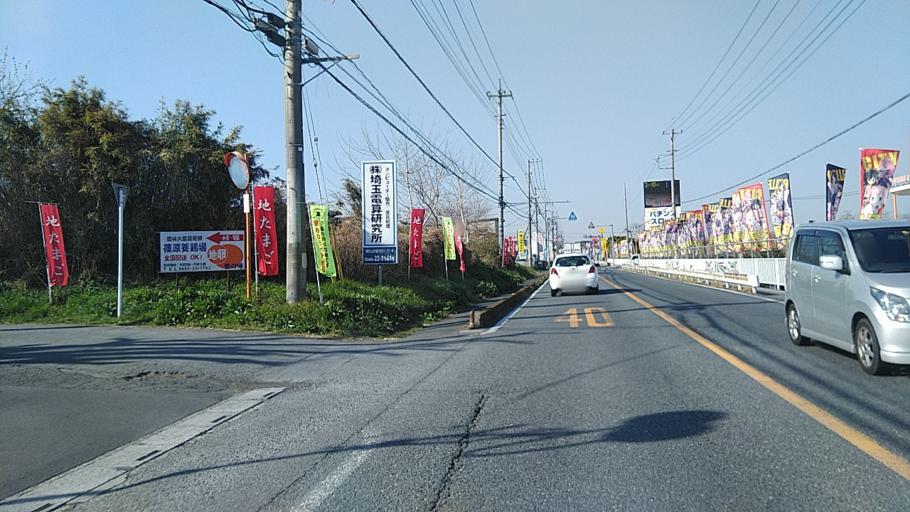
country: JP
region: Saitama
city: Fukiage-fujimi
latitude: 36.0661
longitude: 139.4082
